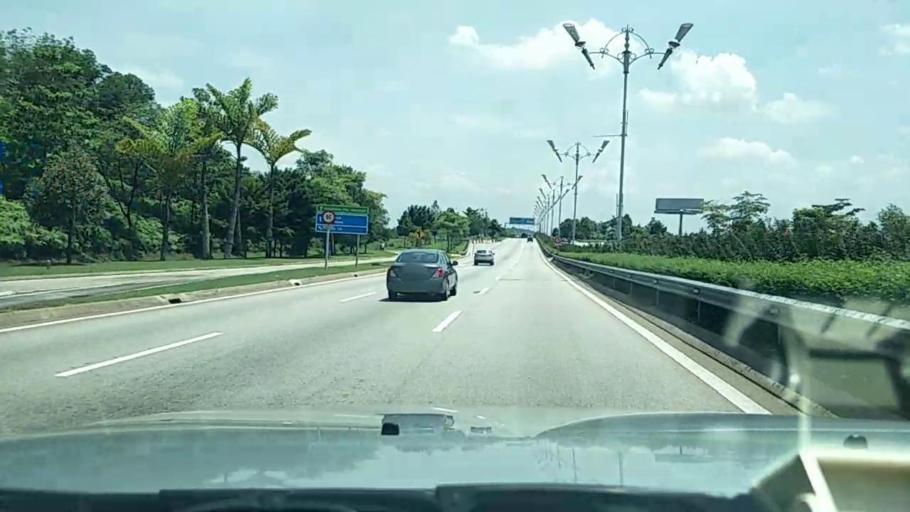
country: MY
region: Putrajaya
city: Putrajaya
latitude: 2.9573
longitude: 101.7093
